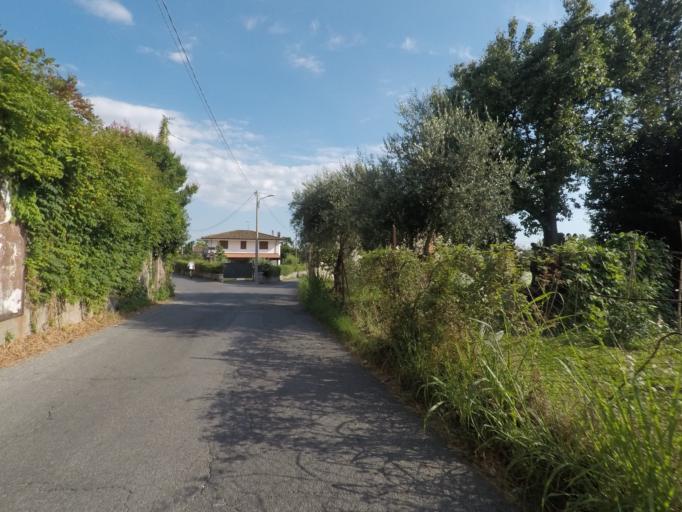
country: IT
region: Tuscany
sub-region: Provincia di Massa-Carrara
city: Capanne-Prato-Cinquale
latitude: 44.0185
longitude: 10.1452
